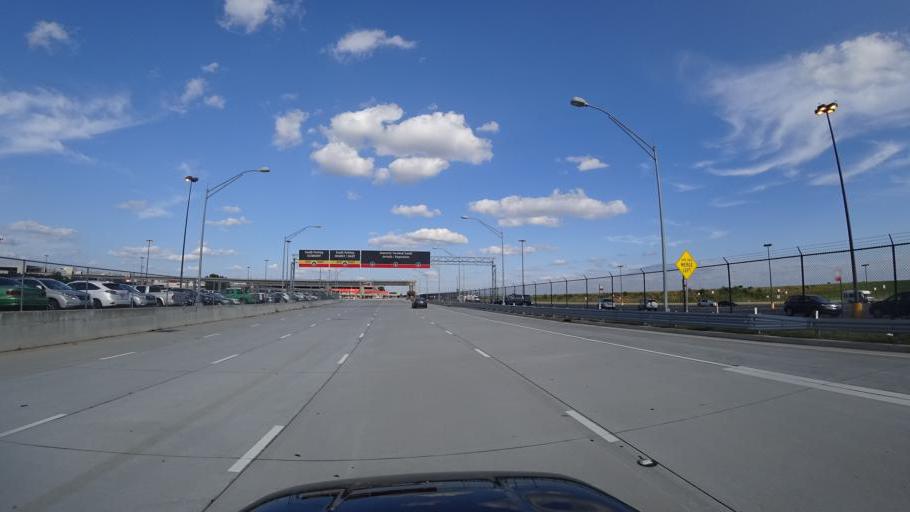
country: US
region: Georgia
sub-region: Fulton County
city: College Park
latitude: 33.6375
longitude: -84.4493
